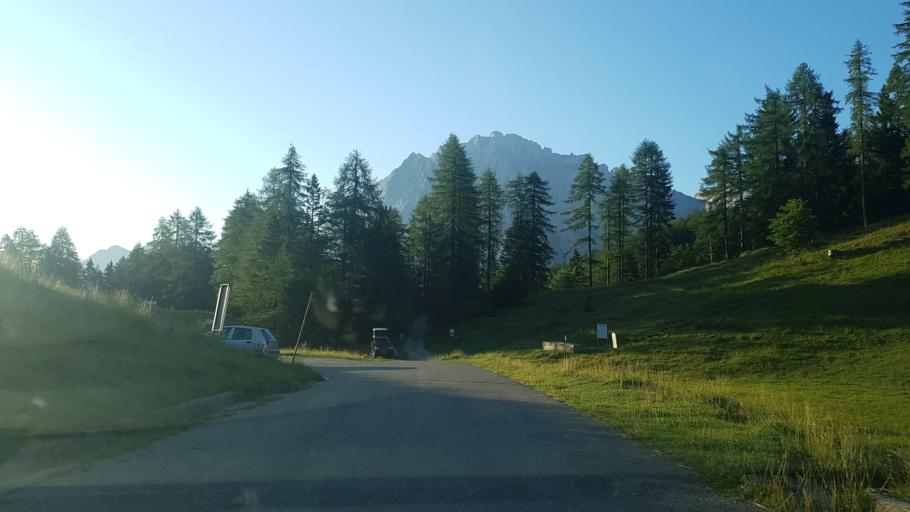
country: IT
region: Friuli Venezia Giulia
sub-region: Provincia di Udine
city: Malborghetto
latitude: 46.4622
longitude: 13.4484
